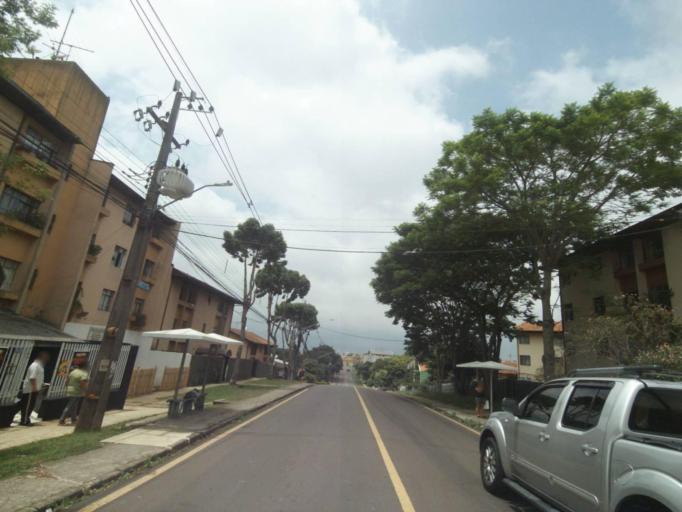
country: BR
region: Parana
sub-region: Curitiba
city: Curitiba
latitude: -25.4876
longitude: -49.3509
